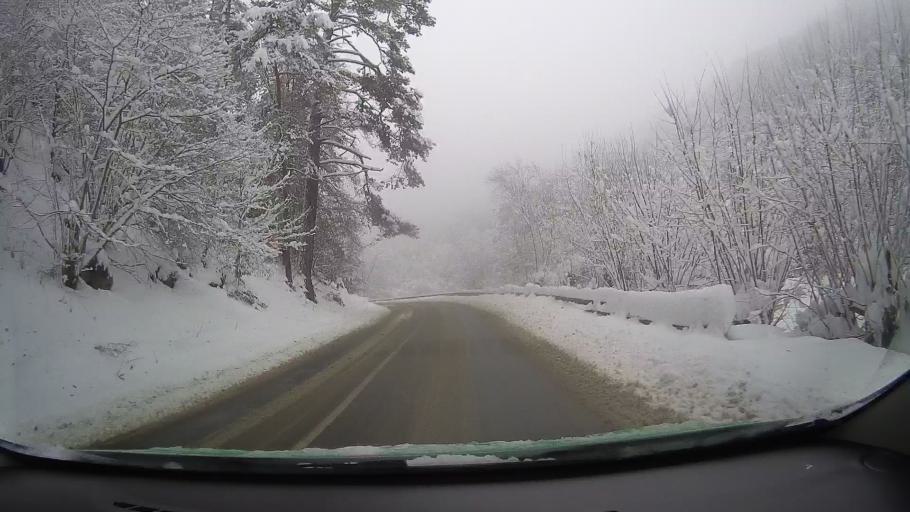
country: RO
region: Sibiu
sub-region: Comuna Tilisca
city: Tilisca
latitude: 45.8017
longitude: 23.8201
